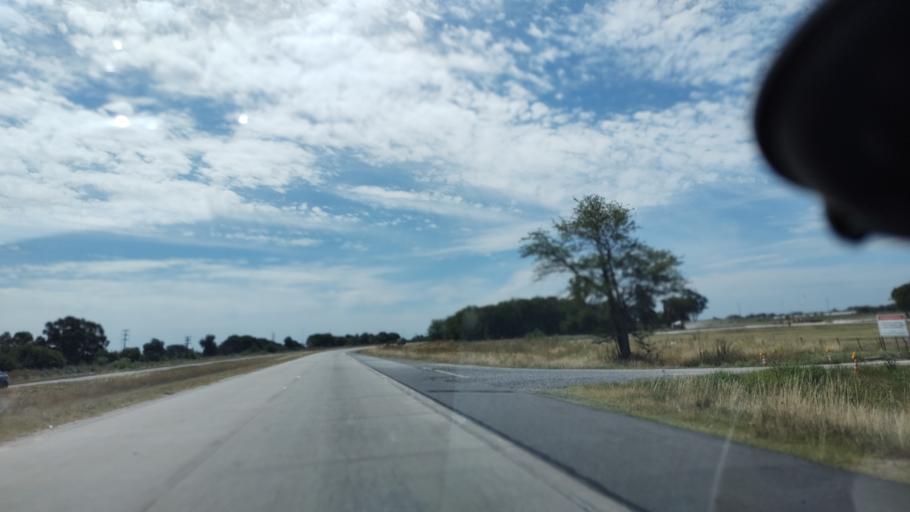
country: AR
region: Buenos Aires
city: Canuelas
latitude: -35.0585
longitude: -58.7068
